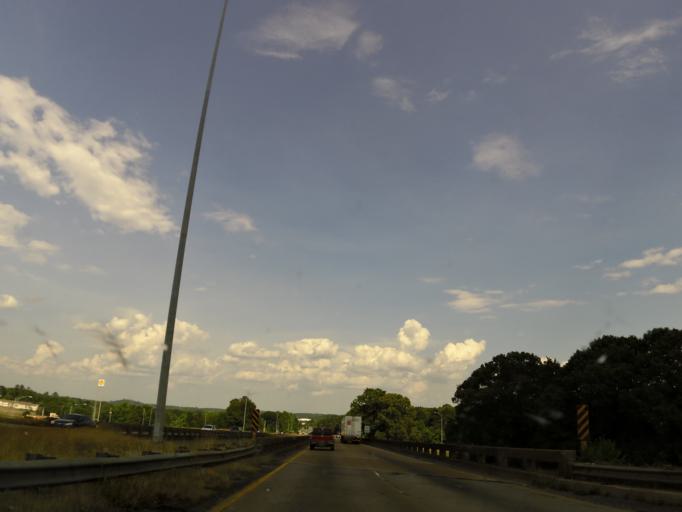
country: US
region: Alabama
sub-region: Tuscaloosa County
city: Holt
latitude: 33.1741
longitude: -87.4754
